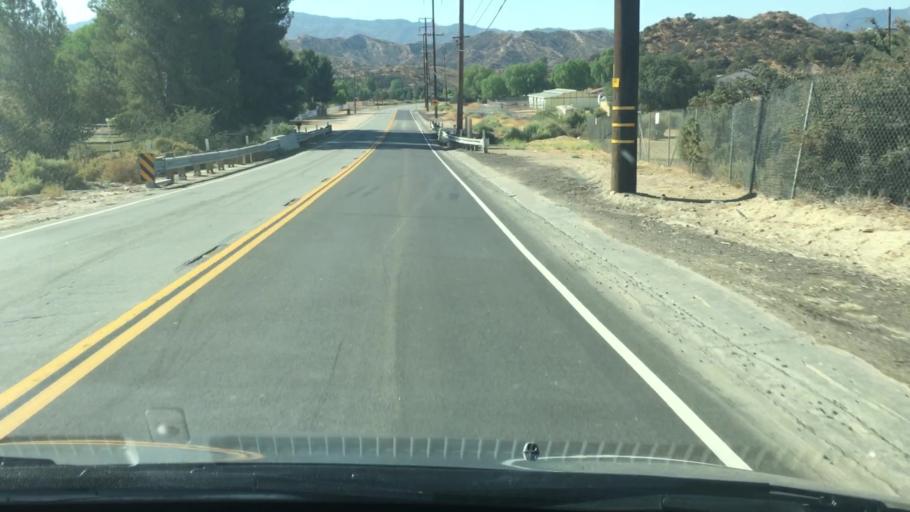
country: US
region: California
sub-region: Los Angeles County
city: Agua Dulce
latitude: 34.4660
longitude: -118.4239
